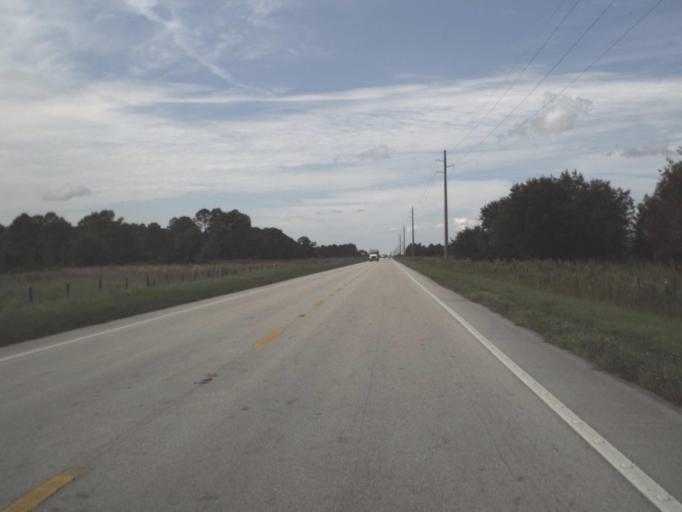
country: US
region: Florida
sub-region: Highlands County
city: Placid Lakes
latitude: 27.2089
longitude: -81.4857
